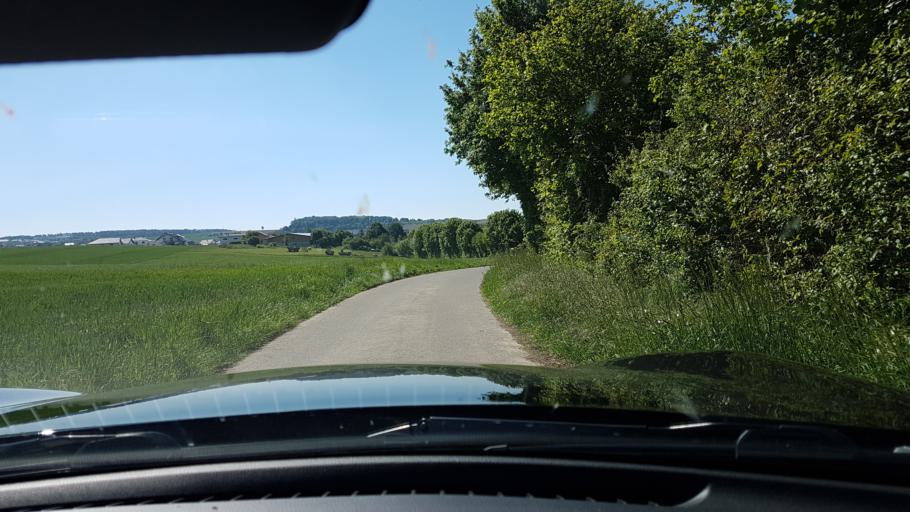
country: DE
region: Baden-Wuerttemberg
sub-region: Karlsruhe Region
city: Osterburken
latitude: 49.4381
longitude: 9.4158
